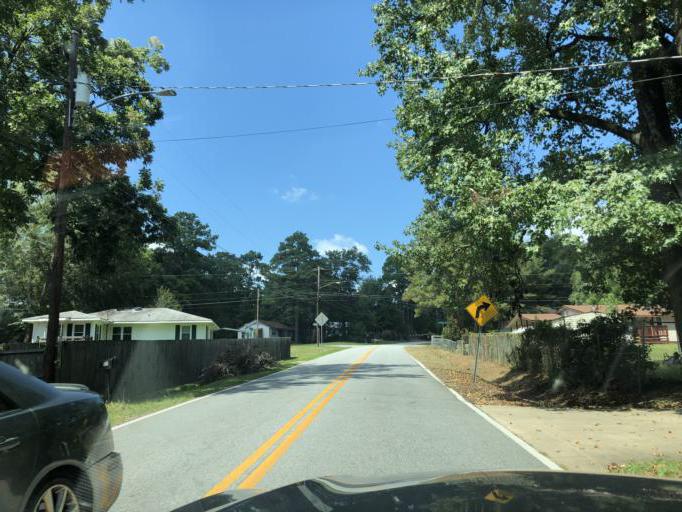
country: US
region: Georgia
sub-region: Muscogee County
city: Columbus
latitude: 32.4849
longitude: -84.9183
